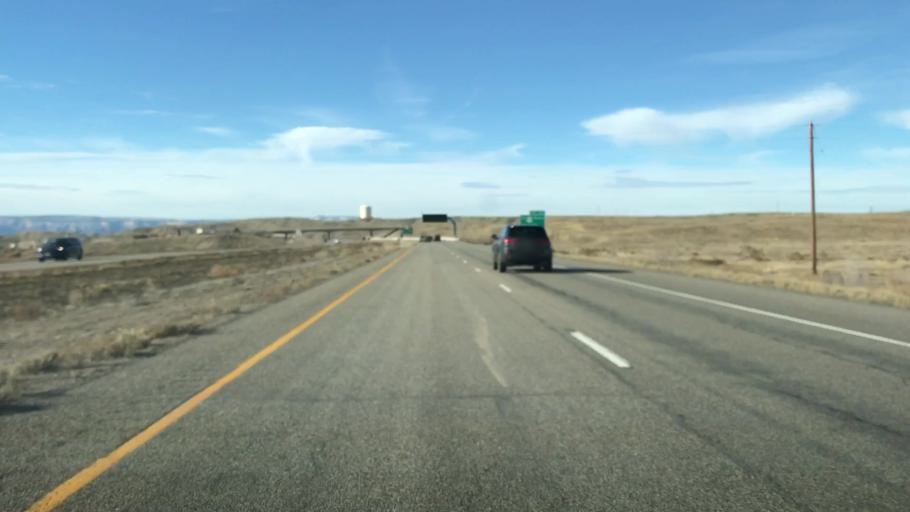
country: US
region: Colorado
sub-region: Mesa County
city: Clifton
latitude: 39.1076
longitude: -108.4356
